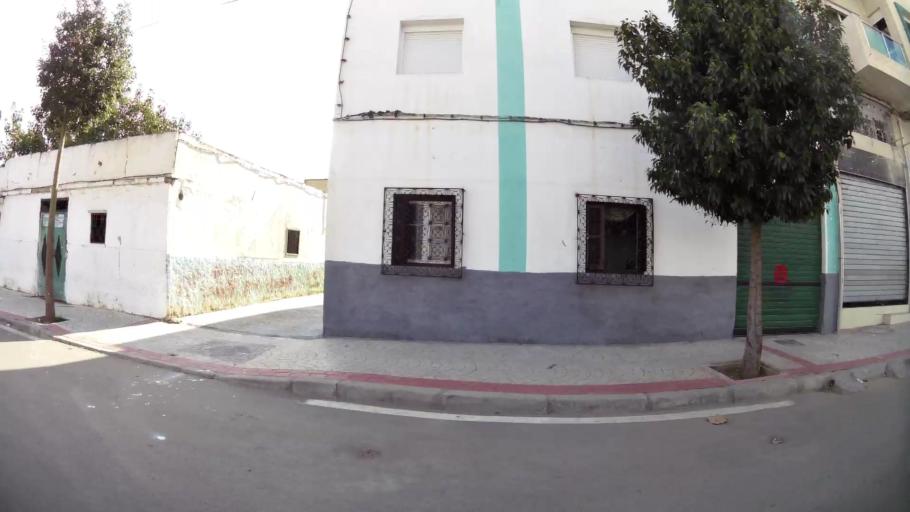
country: MA
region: Tanger-Tetouan
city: Tetouan
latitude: 35.5935
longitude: -5.3471
